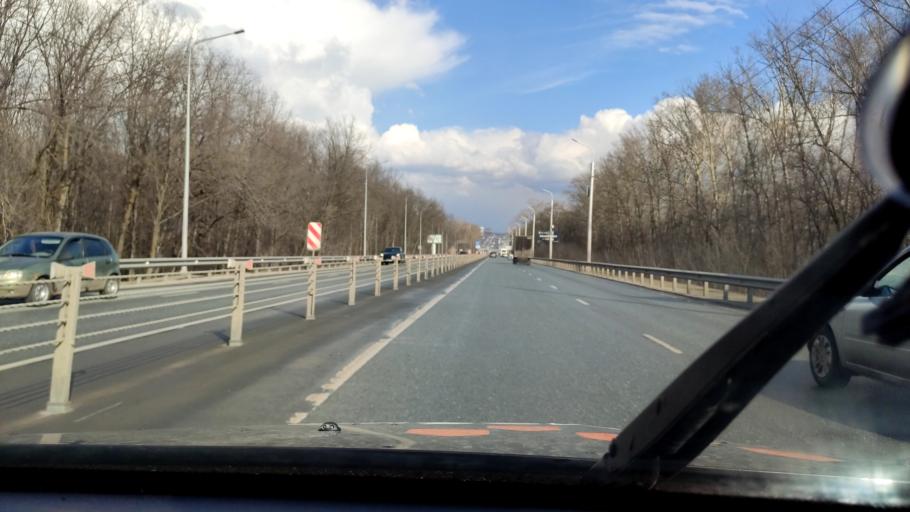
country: RU
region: Bashkortostan
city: Ufa
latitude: 54.6993
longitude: 55.9267
